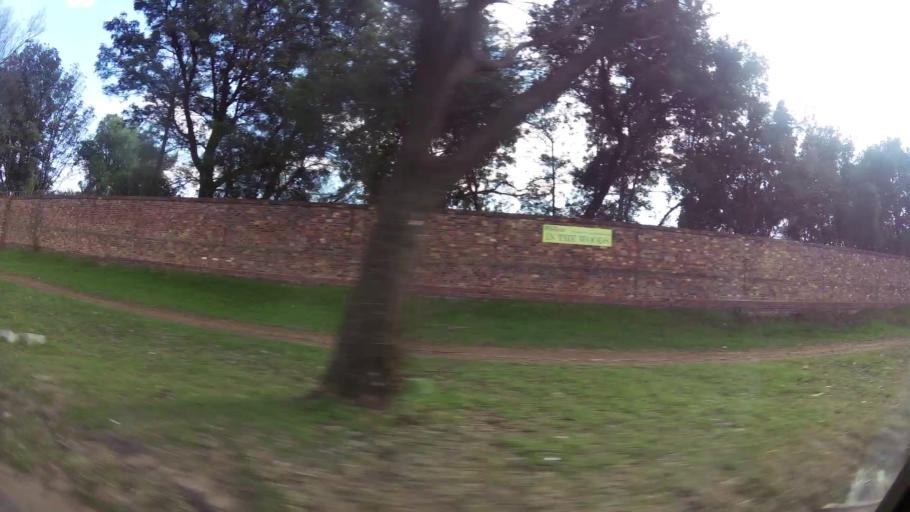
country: ZA
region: Gauteng
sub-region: Ekurhuleni Metropolitan Municipality
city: Germiston
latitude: -26.1946
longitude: 28.1582
